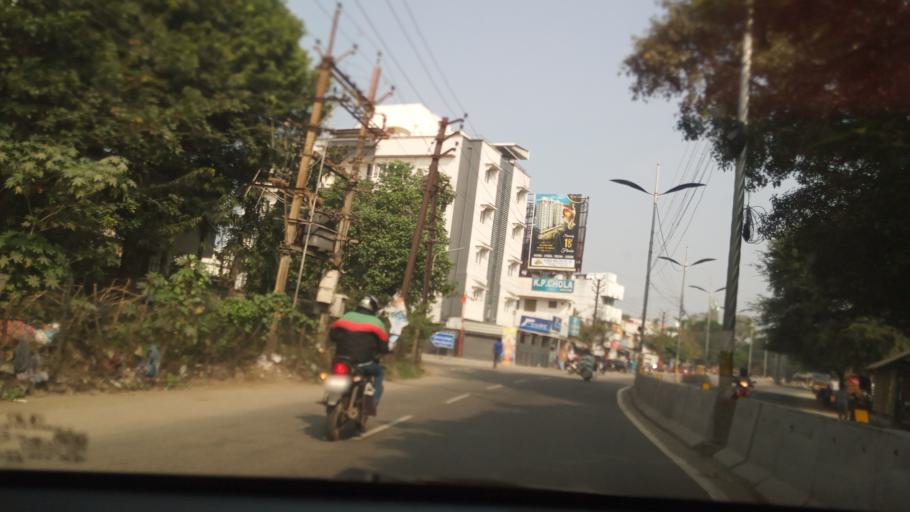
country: IN
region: Tamil Nadu
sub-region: Coimbatore
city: Coimbatore
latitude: 11.0009
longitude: 76.9485
